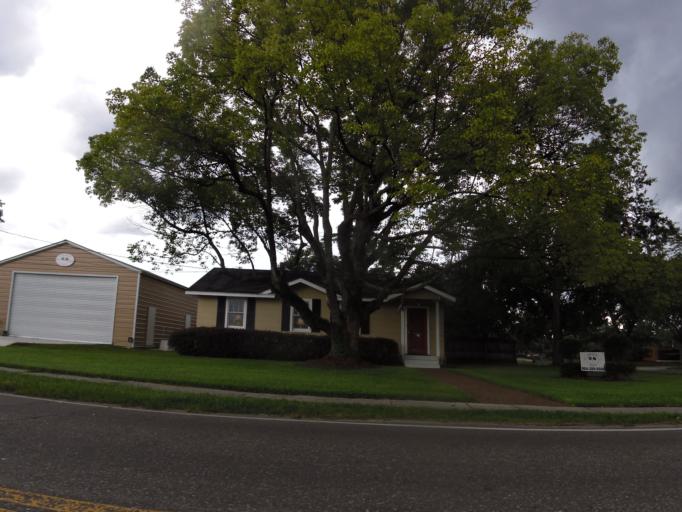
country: US
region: Florida
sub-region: Duval County
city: Jacksonville
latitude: 30.2766
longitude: -81.7180
